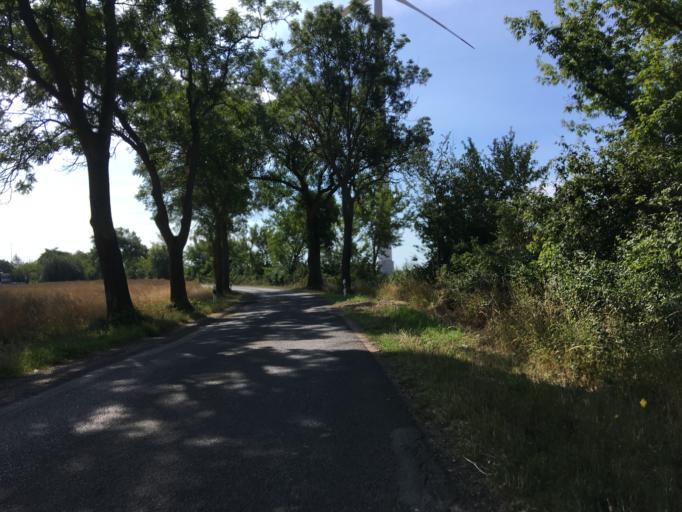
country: DE
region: Brandenburg
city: Gramzow
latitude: 53.2859
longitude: 14.0482
